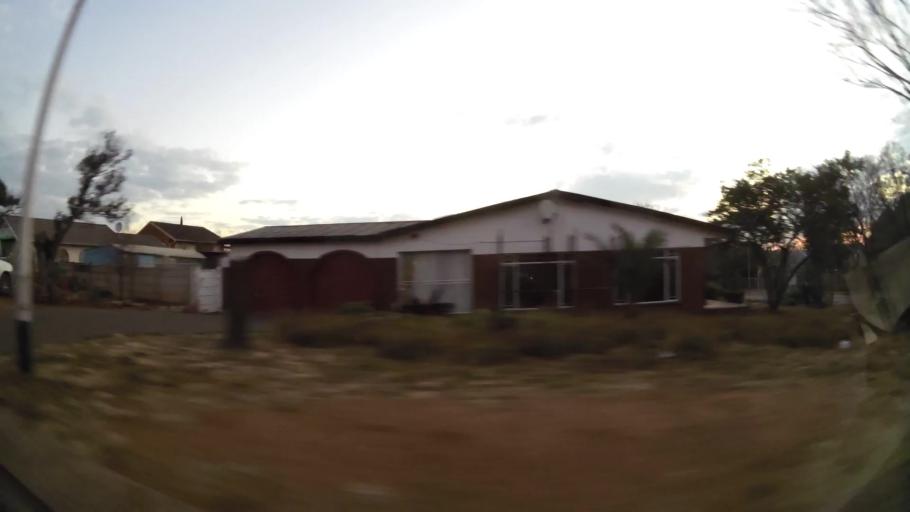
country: ZA
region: Orange Free State
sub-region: Mangaung Metropolitan Municipality
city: Bloemfontein
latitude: -29.1568
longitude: 26.1936
